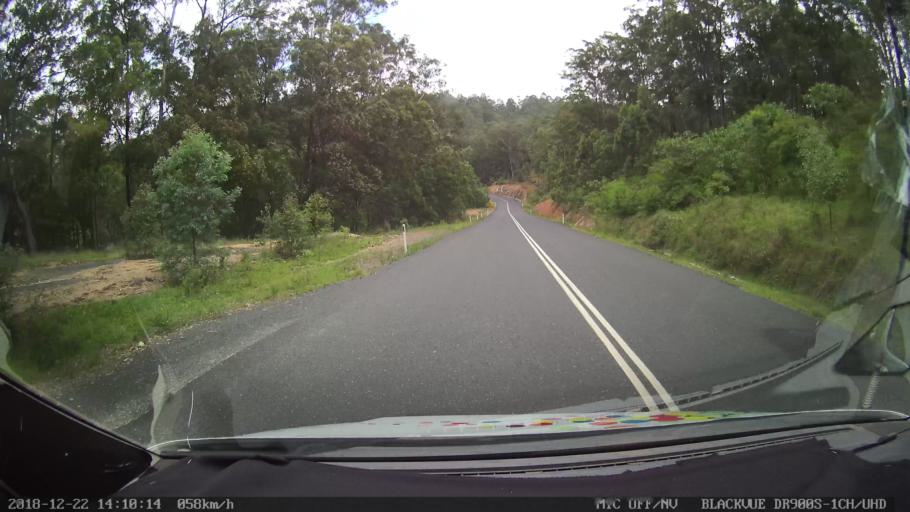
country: AU
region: New South Wales
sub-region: Clarence Valley
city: Coutts Crossing
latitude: -29.9915
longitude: 152.7111
